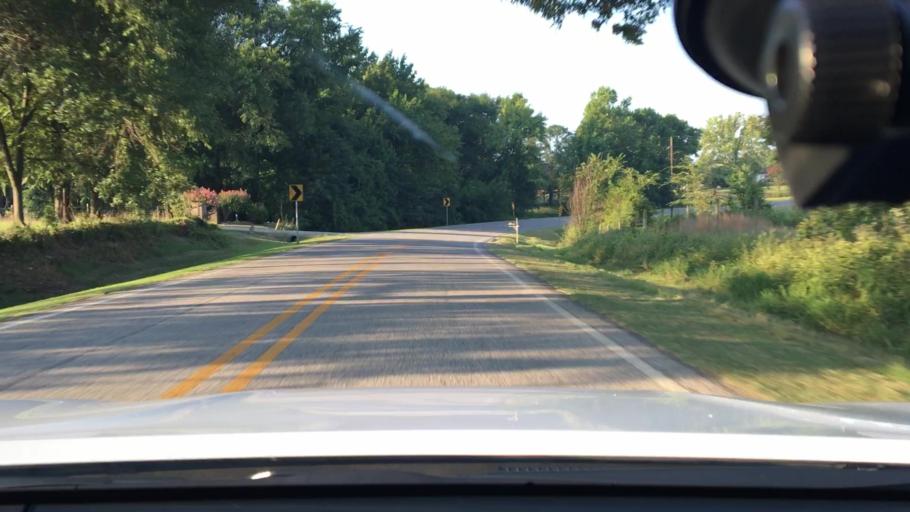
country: US
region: Arkansas
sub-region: Johnson County
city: Coal Hill
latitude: 35.3524
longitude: -93.5664
